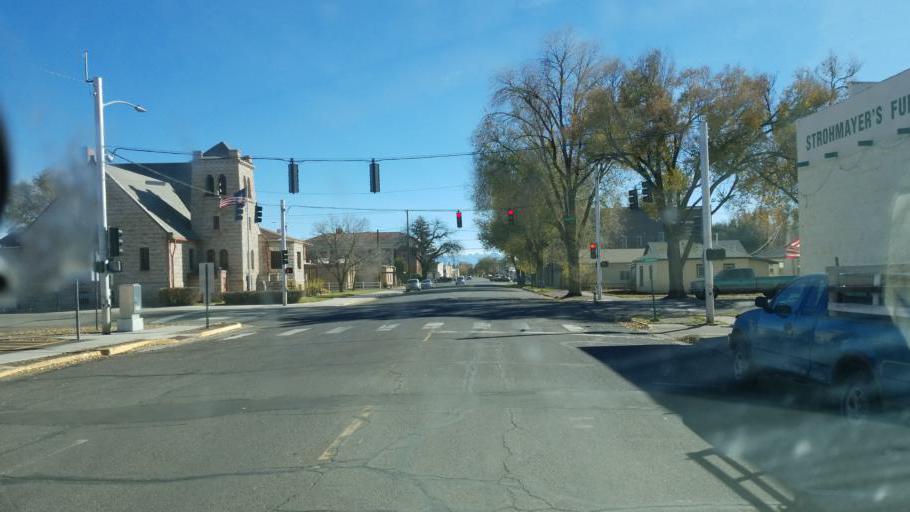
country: US
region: Colorado
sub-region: Rio Grande County
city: Monte Vista
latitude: 37.5793
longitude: -106.1500
